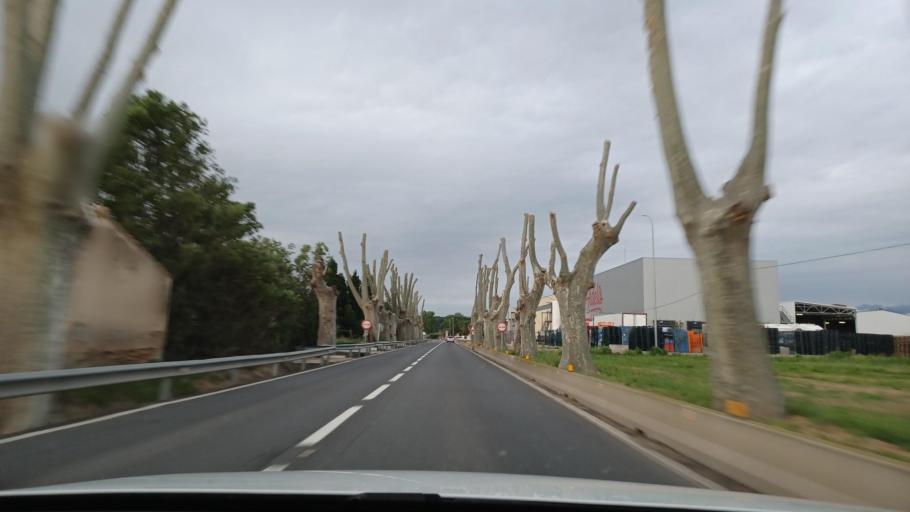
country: ES
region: Catalonia
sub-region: Provincia de Tarragona
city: Tortosa
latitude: 40.7986
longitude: 0.5001
